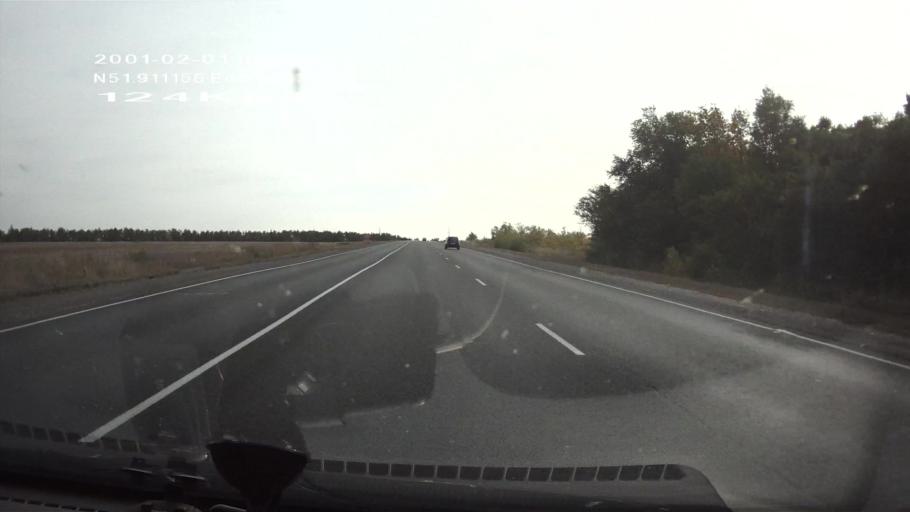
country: RU
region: Saratov
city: Sinodskoye
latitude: 51.9102
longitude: 46.5527
